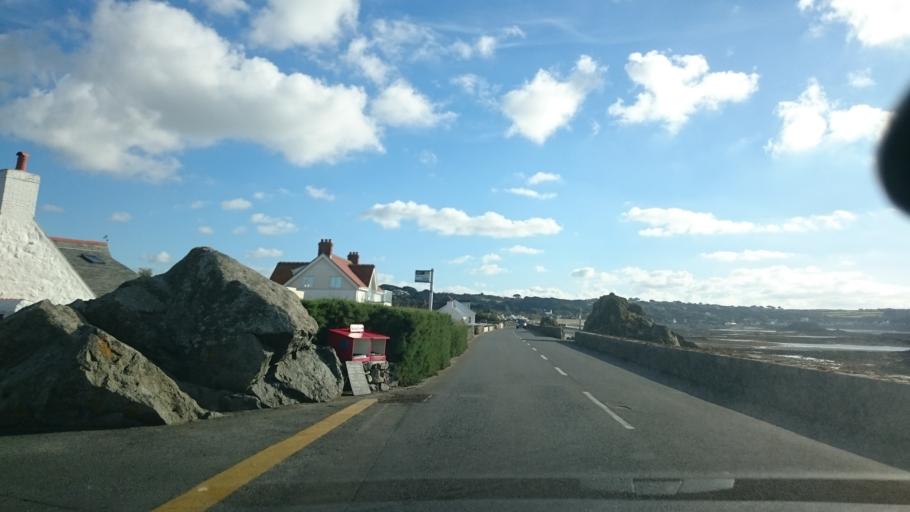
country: GG
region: St Peter Port
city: Saint Peter Port
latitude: 49.4507
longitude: -2.6499
